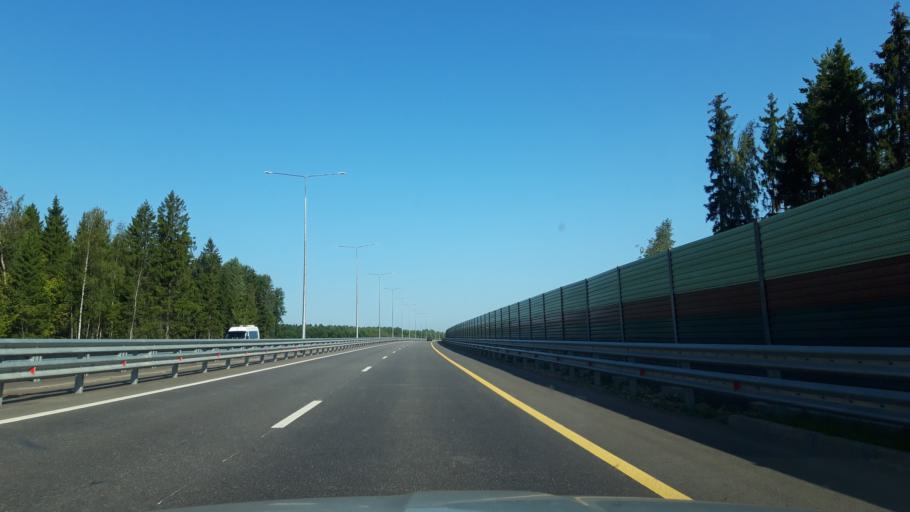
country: RU
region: Tverskaya
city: Zavidovo
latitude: 56.5111
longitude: 36.5110
